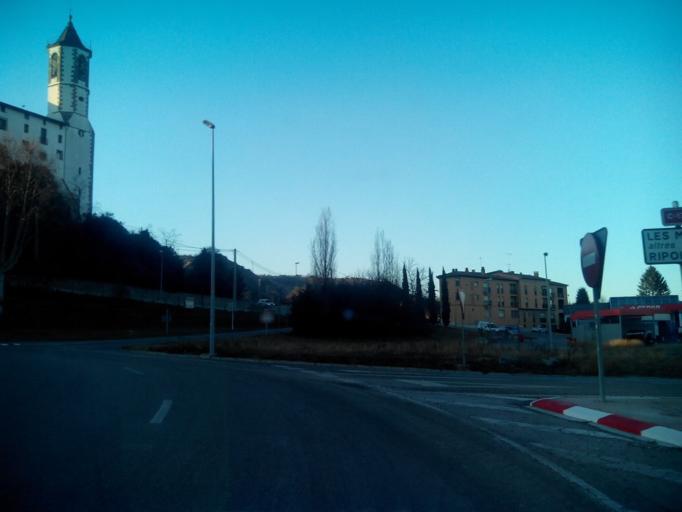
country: ES
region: Catalonia
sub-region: Provincia de Barcelona
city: Santa Cecilia de Voltrega
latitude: 42.0029
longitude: 2.2426
